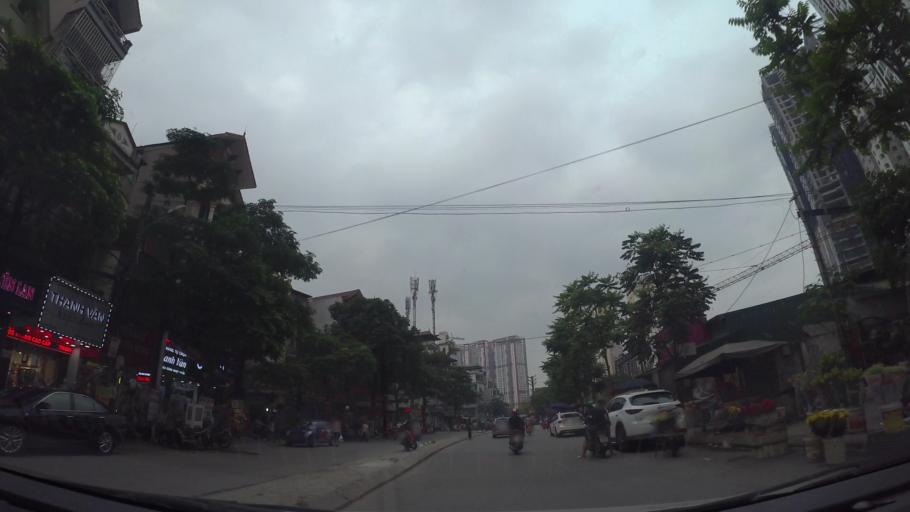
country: VN
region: Ha Noi
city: Cau Dien
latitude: 21.0308
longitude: 105.7767
